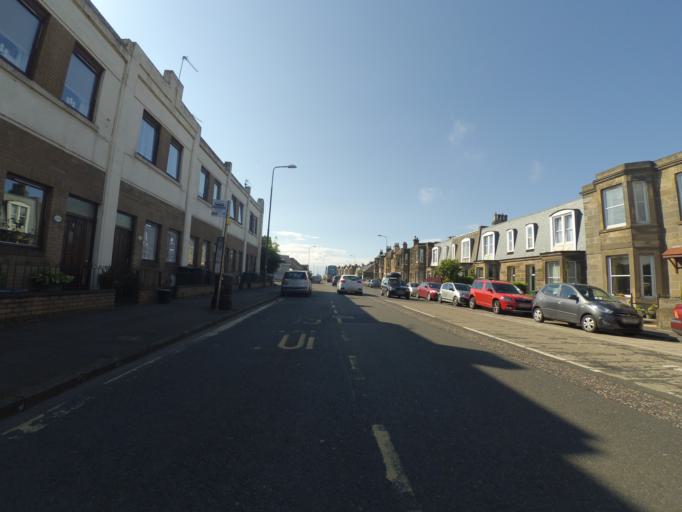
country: GB
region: Scotland
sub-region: East Lothian
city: Musselburgh
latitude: 55.9469
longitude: -3.0810
